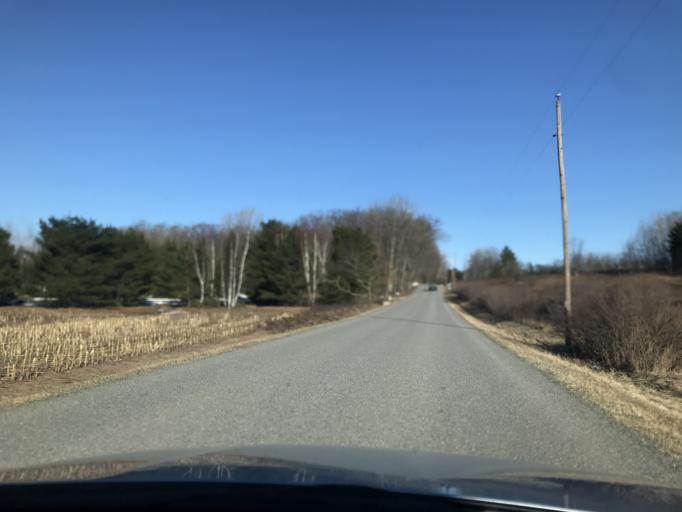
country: US
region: Wisconsin
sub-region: Marinette County
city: Niagara
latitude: 45.3858
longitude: -88.0433
